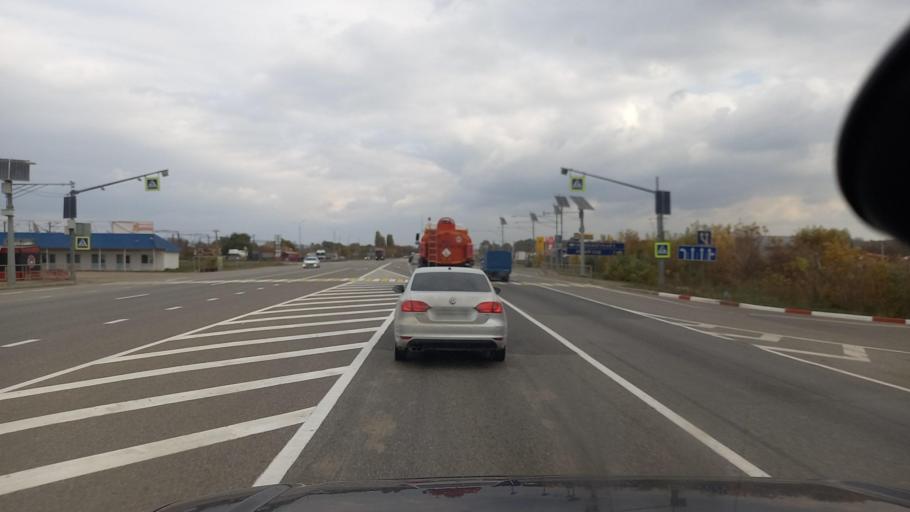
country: RU
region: Adygeya
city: Enem
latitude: 44.9090
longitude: 38.8818
